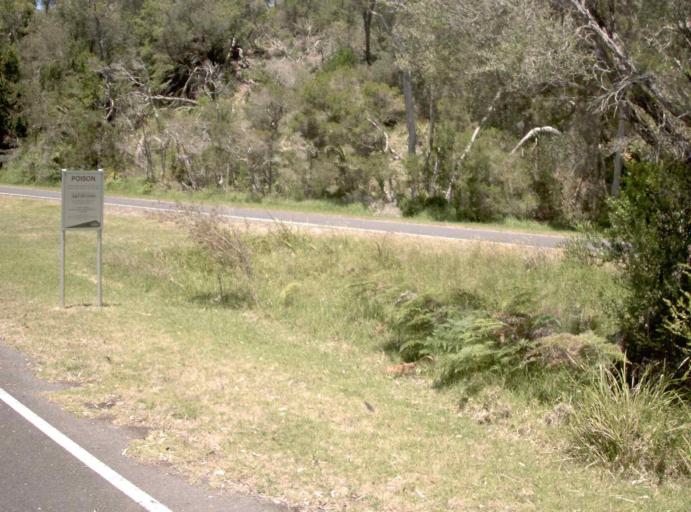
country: AU
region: Victoria
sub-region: Latrobe
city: Morwell
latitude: -38.8588
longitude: 146.2504
